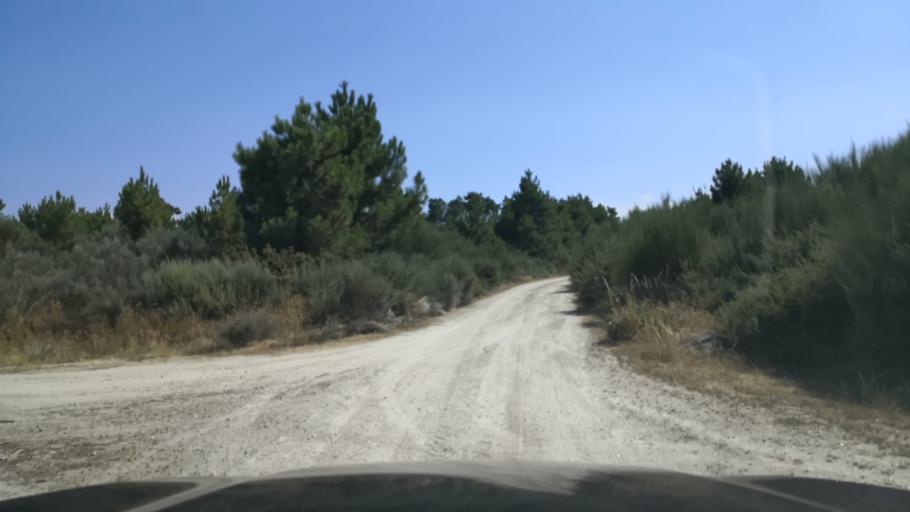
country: PT
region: Vila Real
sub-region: Murca
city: Murca
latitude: 41.3407
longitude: -7.4752
